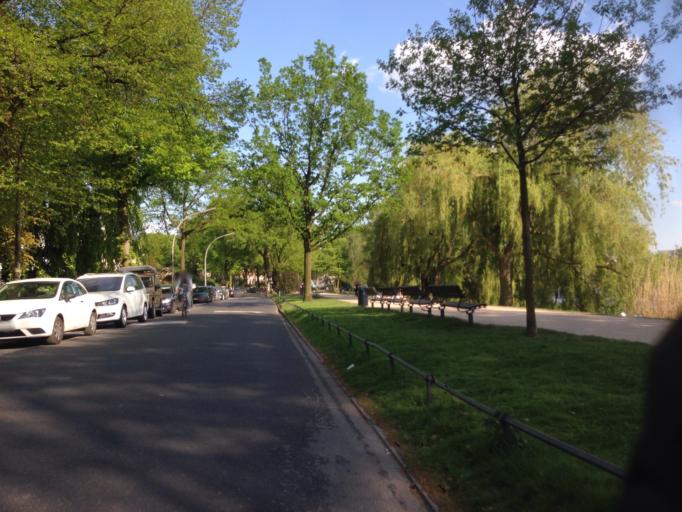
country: DE
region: Hamburg
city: Hamburg
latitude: 53.5692
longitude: 10.0129
